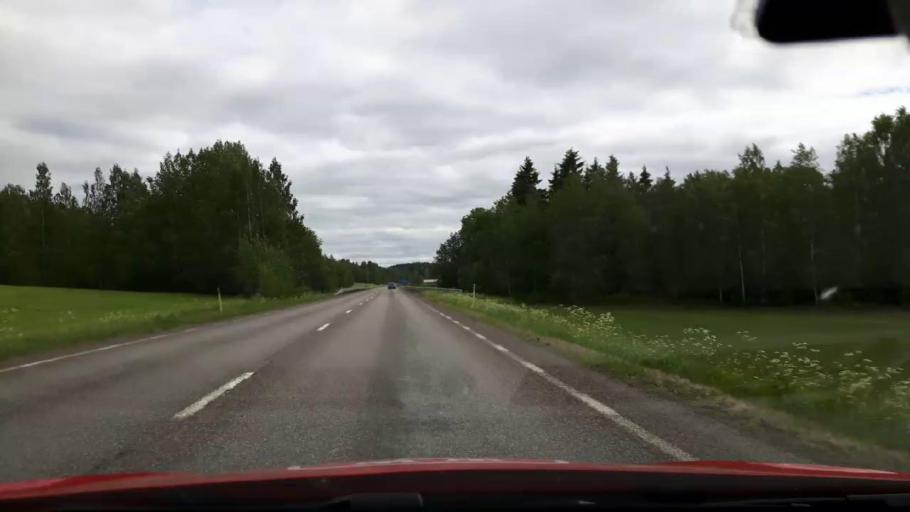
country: SE
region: Jaemtland
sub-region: Ragunda Kommun
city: Hammarstrand
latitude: 63.1255
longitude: 16.3581
